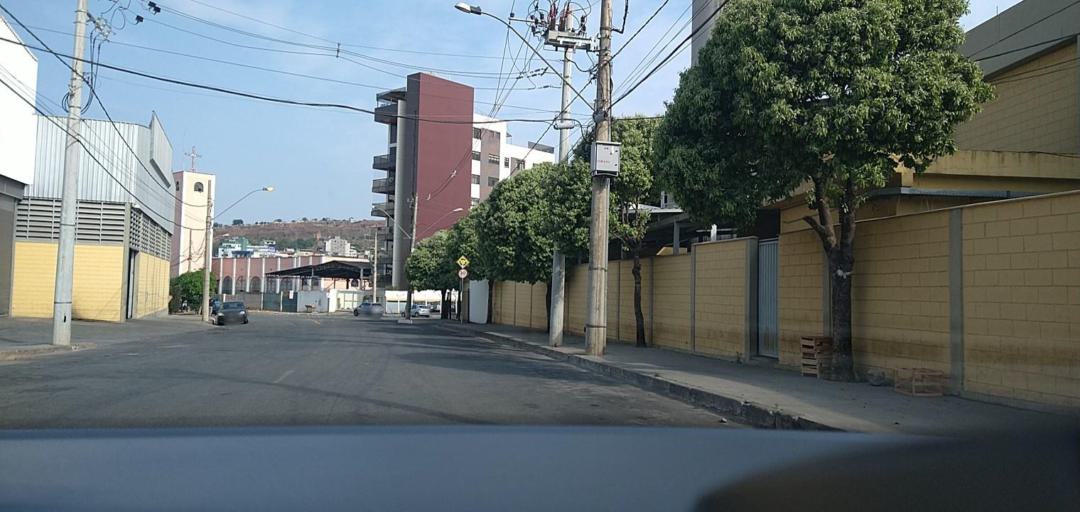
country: BR
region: Minas Gerais
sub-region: Joao Monlevade
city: Joao Monlevade
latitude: -19.8065
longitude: -43.1833
